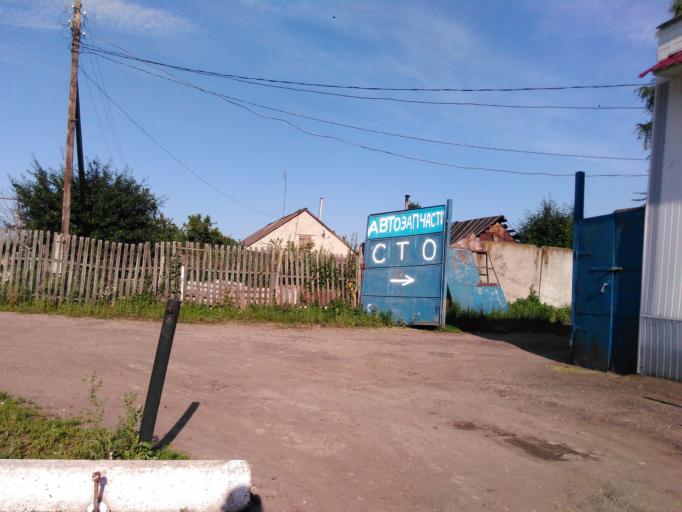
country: RU
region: Penza
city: Lermontovo
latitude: 52.9940
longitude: 43.6591
